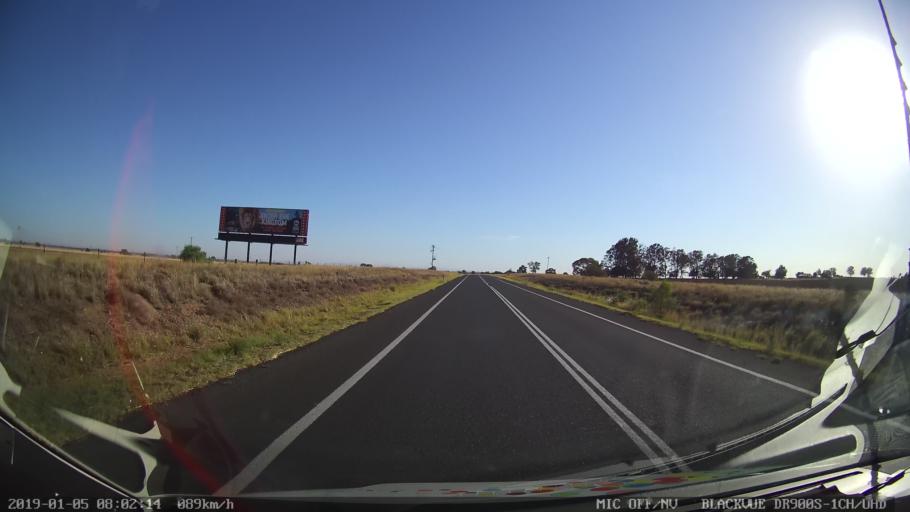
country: AU
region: New South Wales
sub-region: Gilgandra
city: Gilgandra
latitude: -31.6778
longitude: 148.7091
